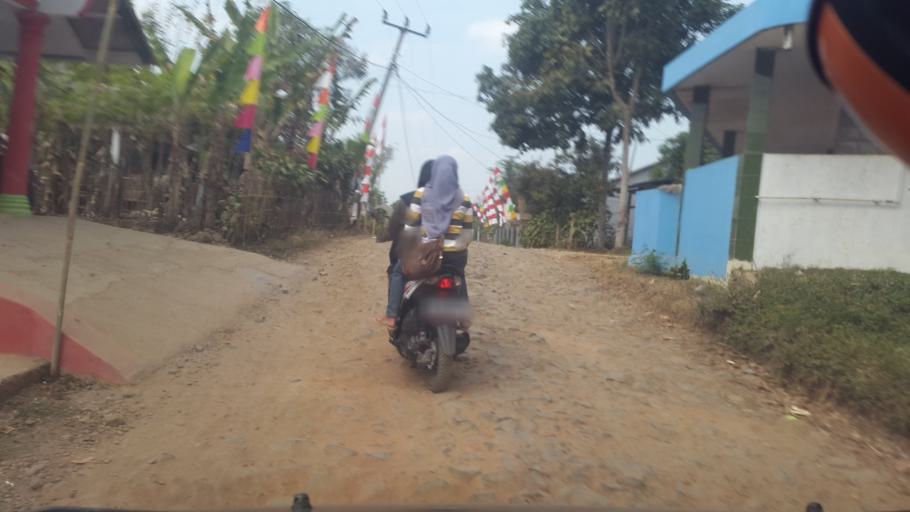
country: ID
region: West Java
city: Nangerang
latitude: -7.1083
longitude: 106.7798
